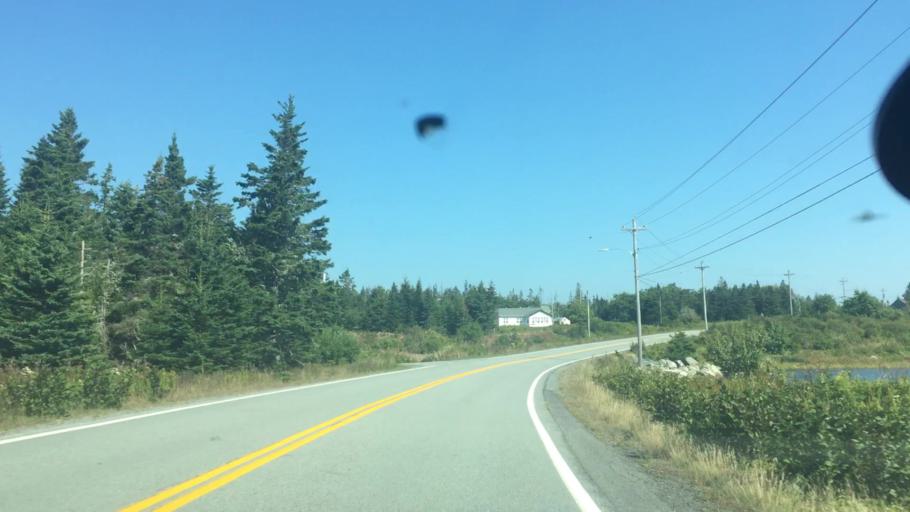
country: CA
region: Nova Scotia
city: New Glasgow
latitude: 44.9198
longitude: -62.3048
